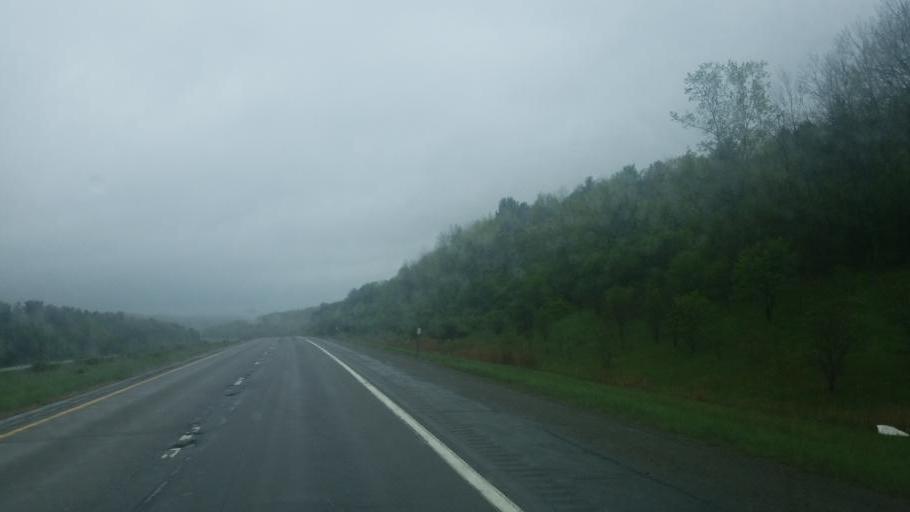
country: US
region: New York
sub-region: Allegany County
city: Alfred
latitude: 42.3036
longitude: -77.9067
